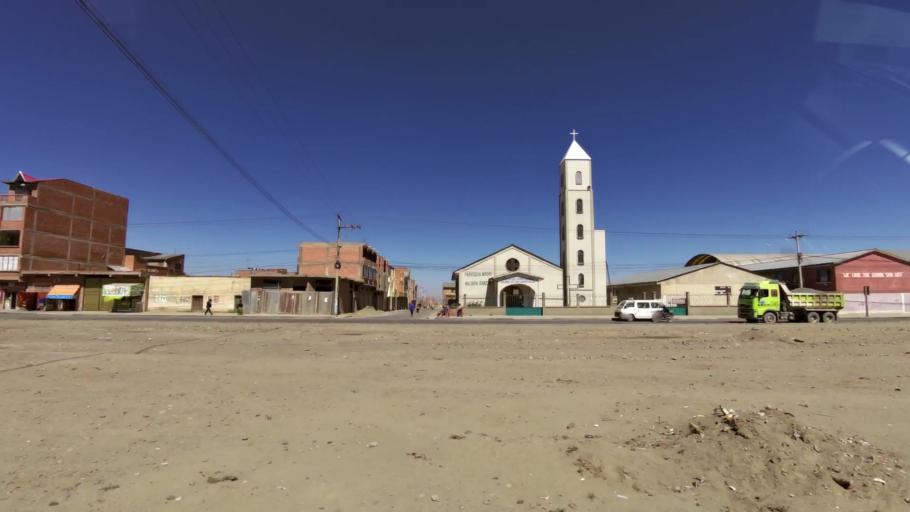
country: BO
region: La Paz
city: La Paz
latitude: -16.5424
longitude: -68.2006
